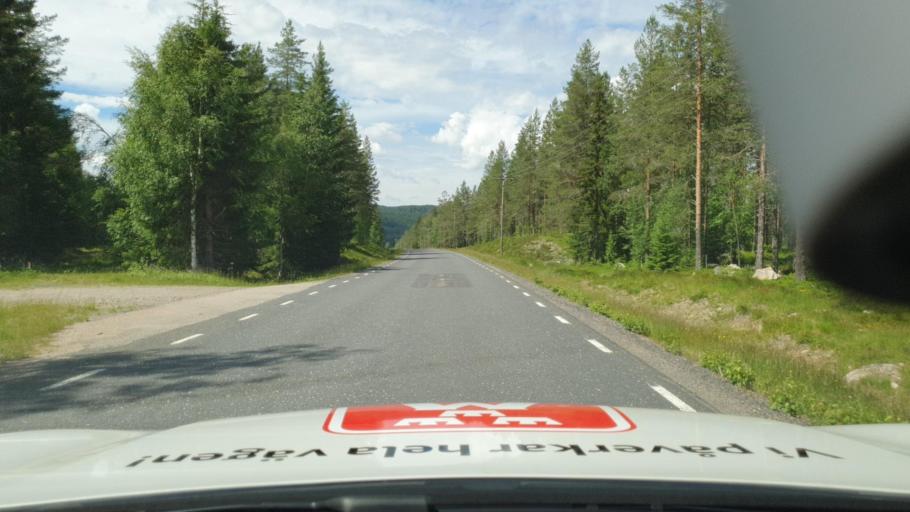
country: SE
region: Vaermland
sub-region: Torsby Kommun
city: Torsby
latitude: 60.5608
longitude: 12.7591
